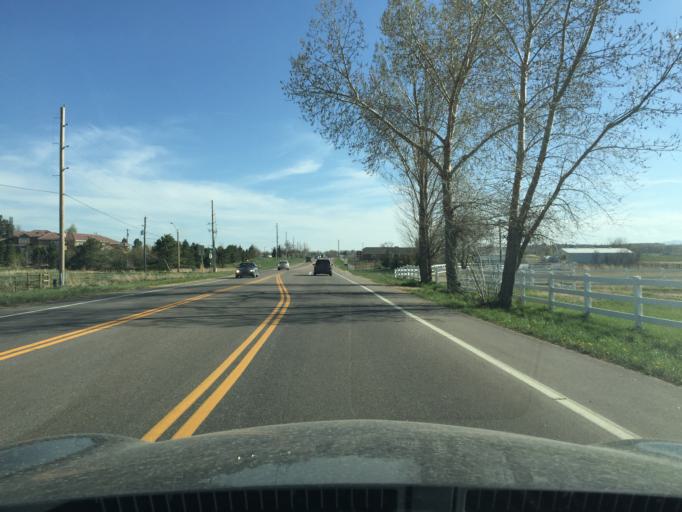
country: US
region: Colorado
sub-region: Boulder County
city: Niwot
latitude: 40.1172
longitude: -105.1311
